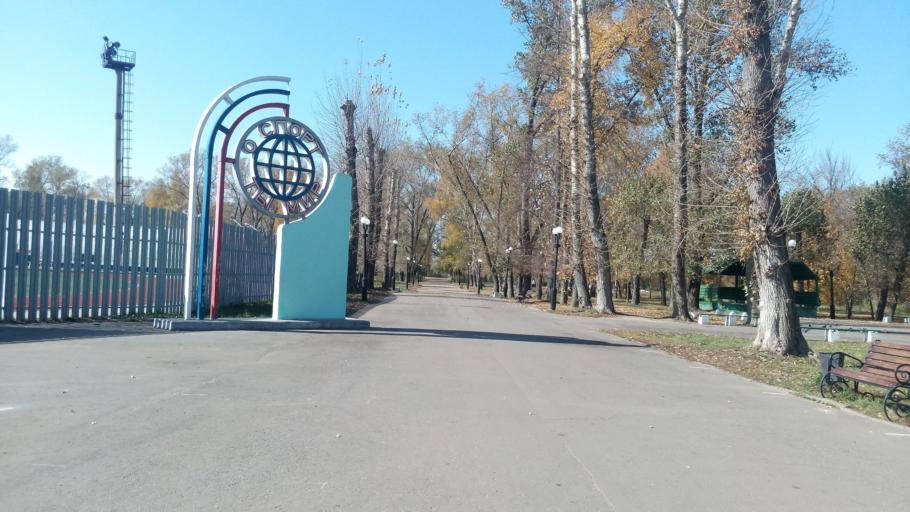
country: RU
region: Tambov
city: Kotovsk
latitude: 52.5860
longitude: 41.4952
